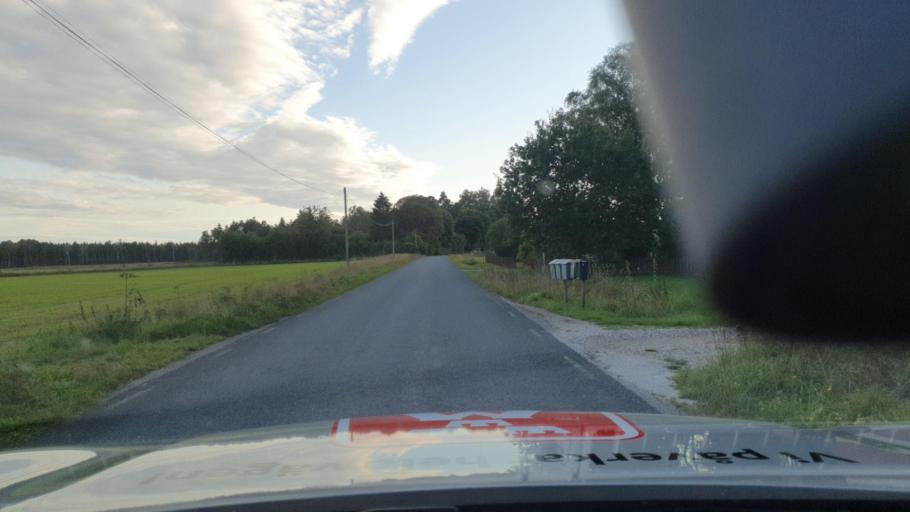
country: SE
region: Gotland
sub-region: Gotland
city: Hemse
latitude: 57.4276
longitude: 18.4188
